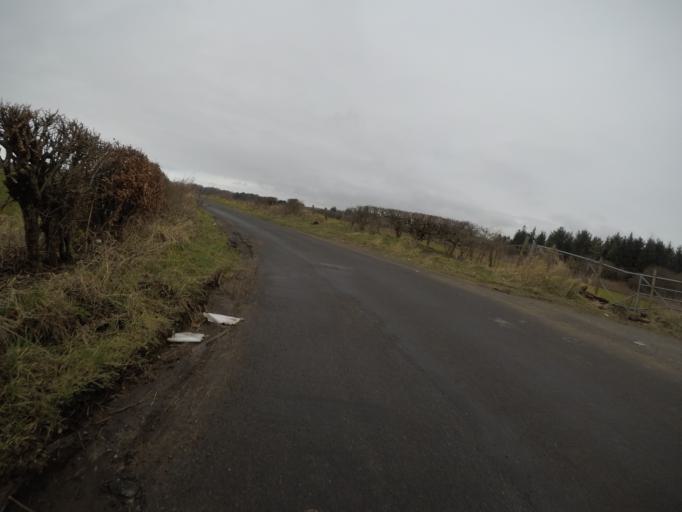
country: GB
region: Scotland
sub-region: North Ayrshire
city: Kilwinning
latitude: 55.6444
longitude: -4.7097
